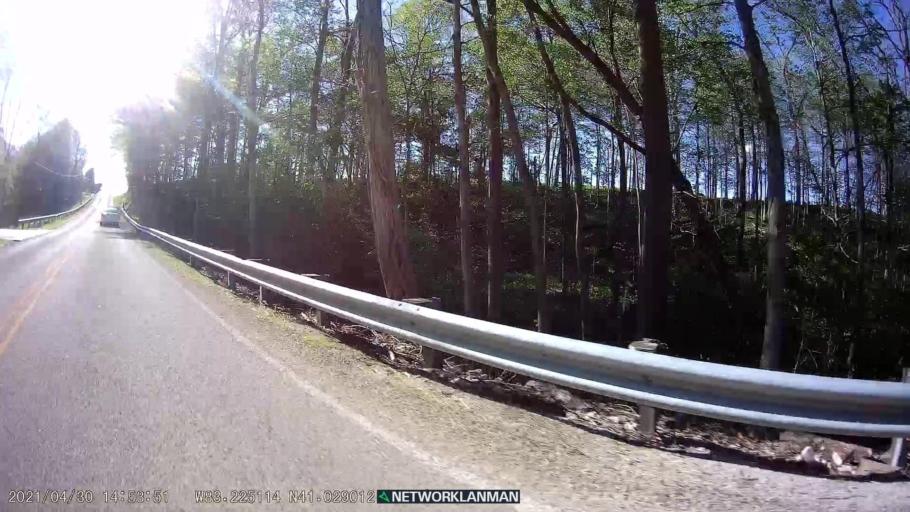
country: US
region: Ohio
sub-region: Seneca County
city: Tiffin
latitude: 41.0289
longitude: -83.2254
